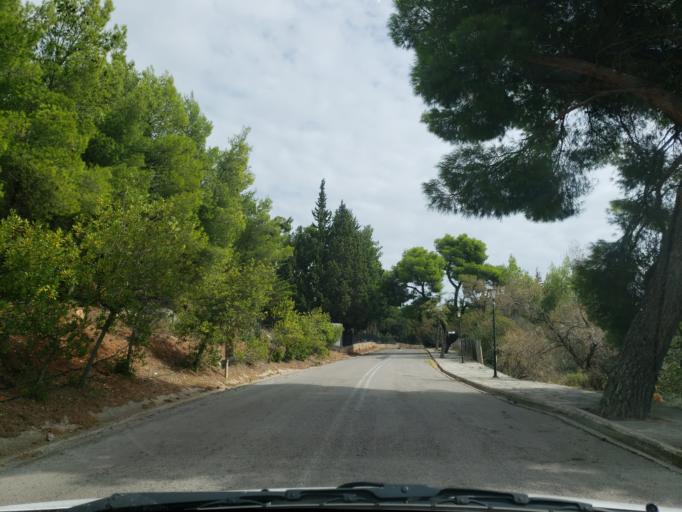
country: GR
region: Central Greece
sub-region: Nomos Fokidos
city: Delphi
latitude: 38.4817
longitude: 22.4882
